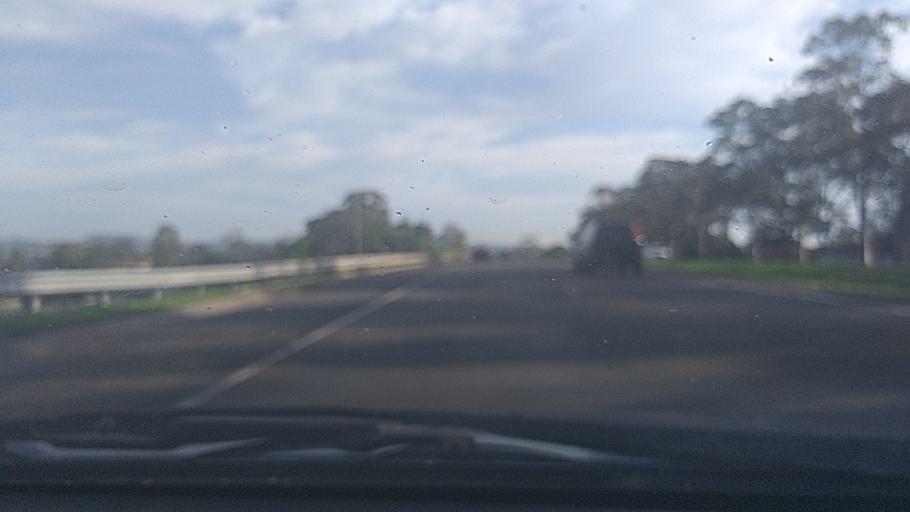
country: AU
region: New South Wales
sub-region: Campbelltown Municipality
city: Glen Alpine
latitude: -34.0918
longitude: 150.8052
